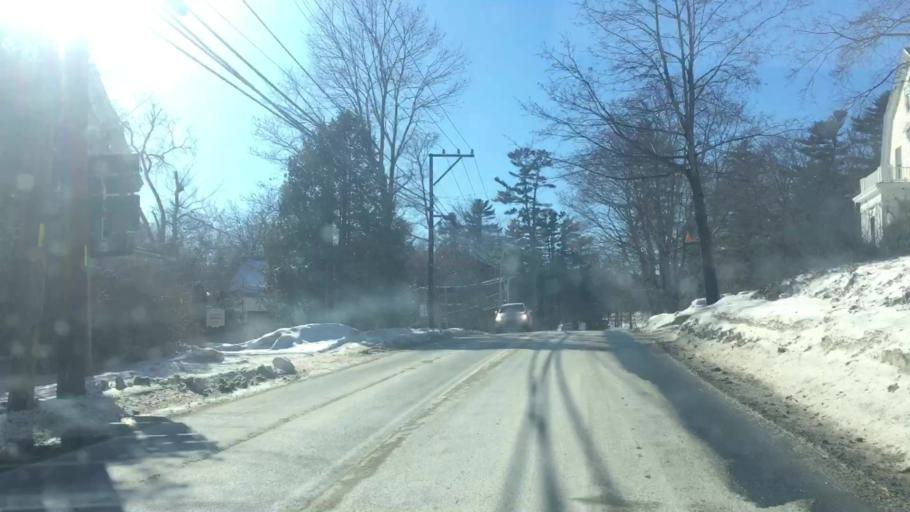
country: US
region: Maine
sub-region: Hancock County
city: Ellsworth
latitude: 44.5382
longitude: -68.4297
